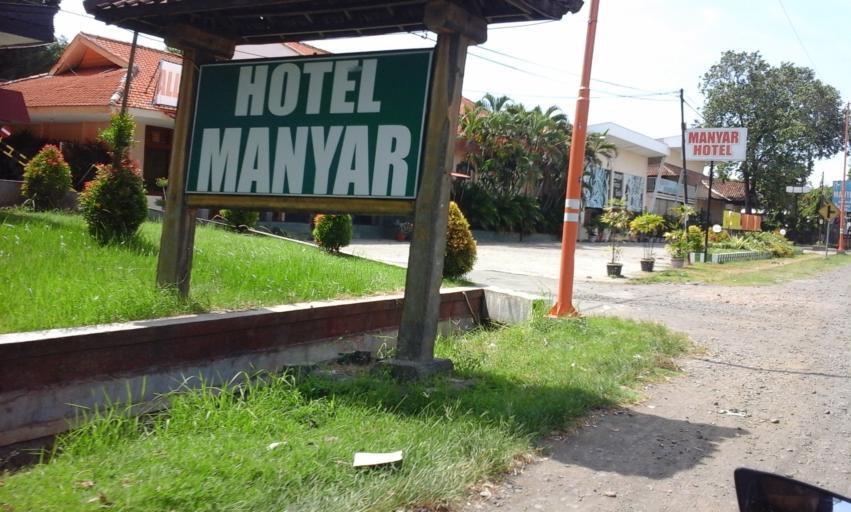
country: ID
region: East Java
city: Klatakan
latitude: -8.1507
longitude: 114.3977
